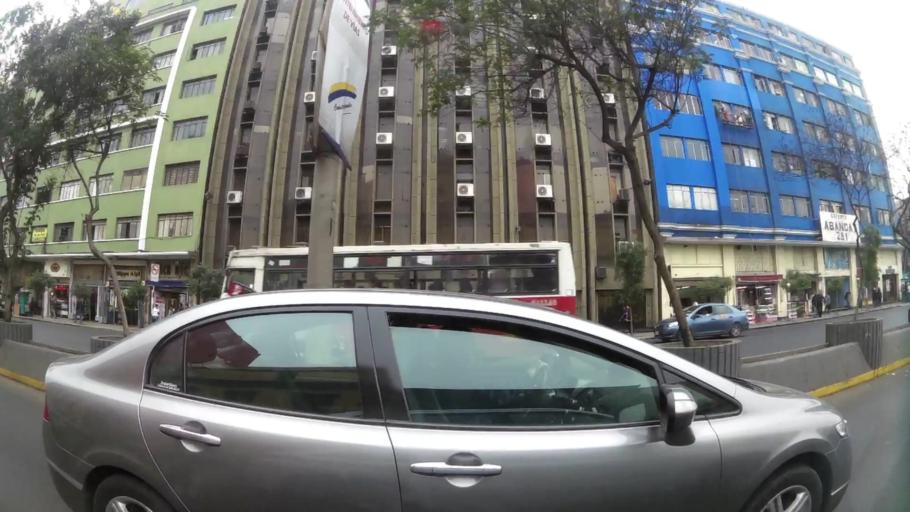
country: PE
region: Lima
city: Lima
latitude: -12.0483
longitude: -77.0271
